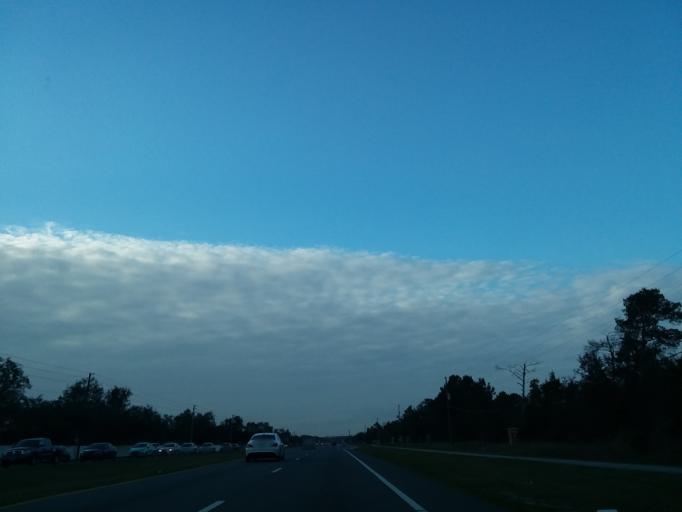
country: US
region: Florida
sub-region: Osceola County
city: Poinciana
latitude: 28.1685
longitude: -81.4403
